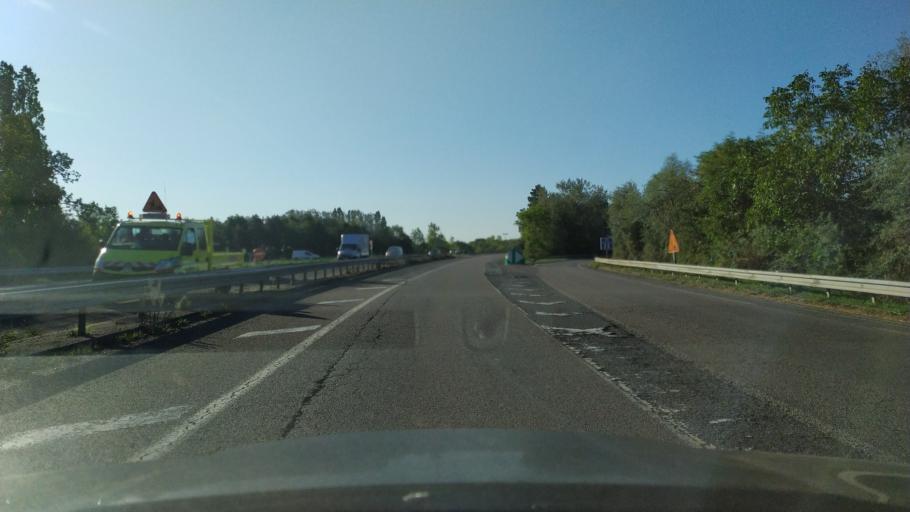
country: FR
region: Lorraine
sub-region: Departement de la Moselle
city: Moulins-les-Metz
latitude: 49.0992
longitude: 6.1168
